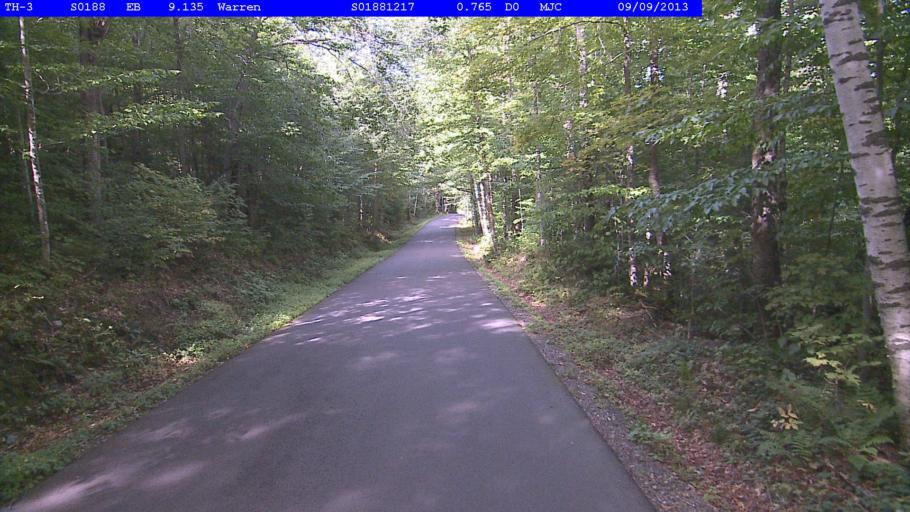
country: US
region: Vermont
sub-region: Addison County
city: Bristol
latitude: 44.0929
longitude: -72.9111
